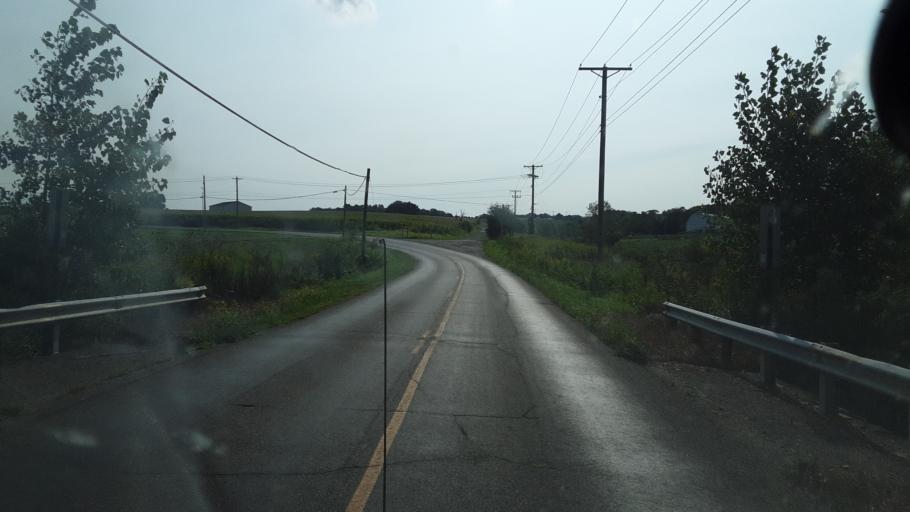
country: US
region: Ohio
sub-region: Knox County
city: Danville
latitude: 40.4442
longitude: -82.3023
